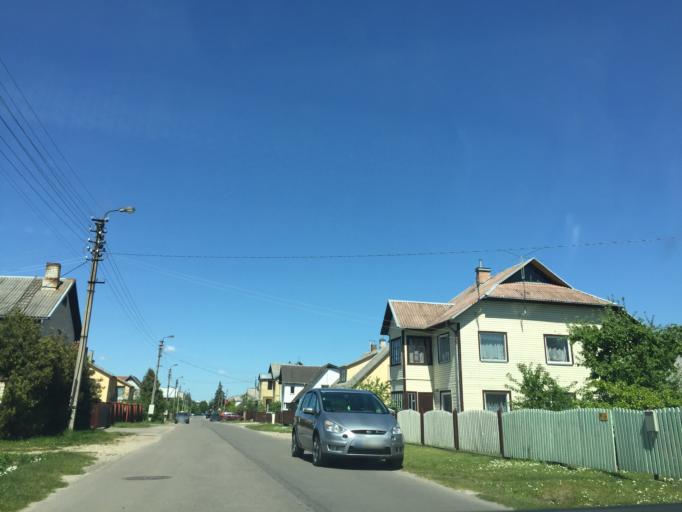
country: LT
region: Panevezys
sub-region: Panevezys City
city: Panevezys
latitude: 55.7202
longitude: 24.3743
